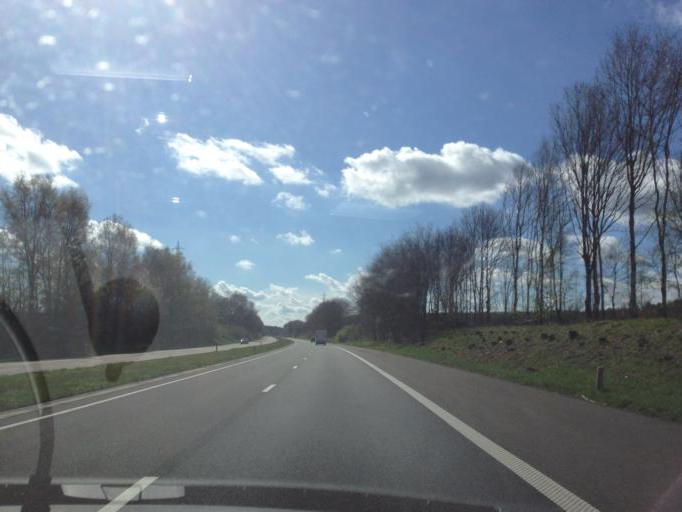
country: BE
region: Flanders
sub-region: Provincie Limburg
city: Overpelt
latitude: 51.1802
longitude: 5.3943
